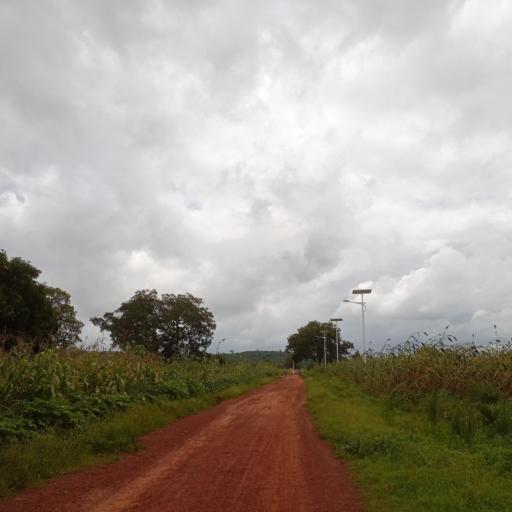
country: TG
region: Savanes
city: Dapaong
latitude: 10.7959
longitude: -0.0159
